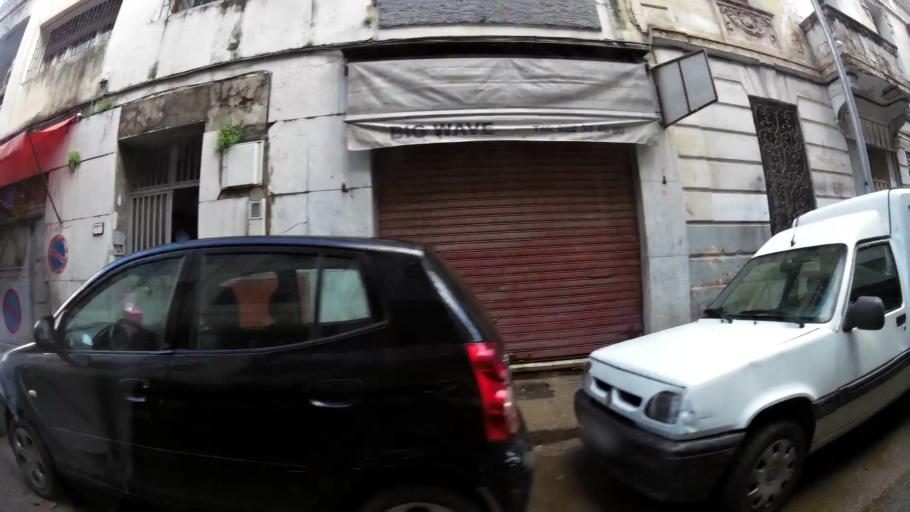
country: MA
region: Grand Casablanca
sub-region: Casablanca
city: Casablanca
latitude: 33.5886
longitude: -7.6134
